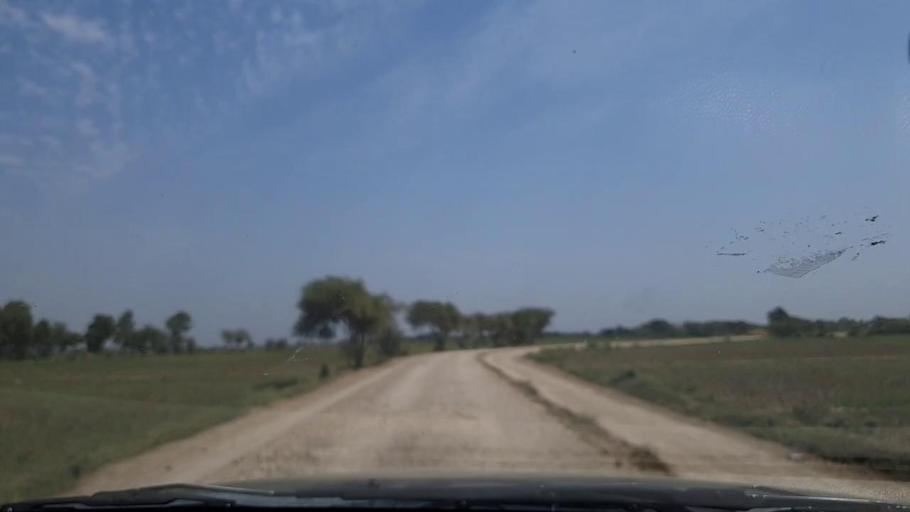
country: PK
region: Sindh
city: Mirpur Batoro
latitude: 24.6422
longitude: 68.1585
